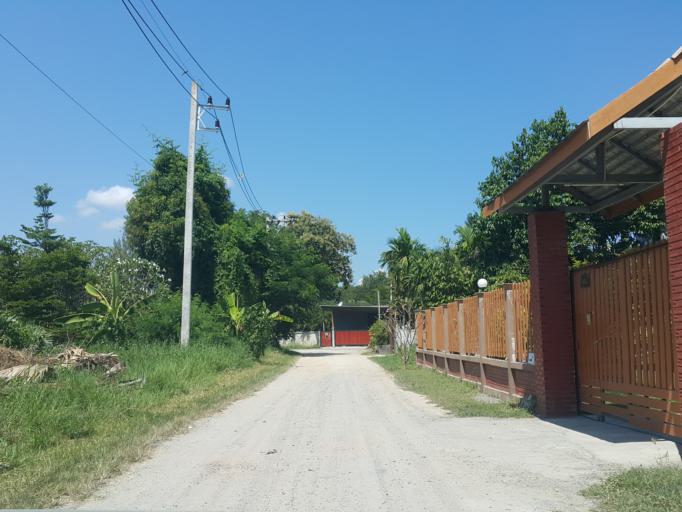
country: TH
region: Chiang Mai
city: Saraphi
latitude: 18.7617
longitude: 99.0483
